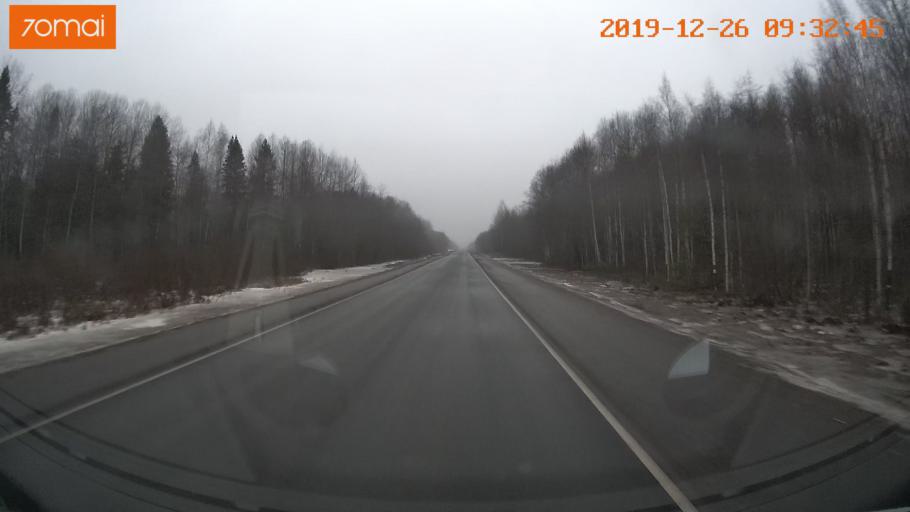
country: RU
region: Vologda
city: Gryazovets
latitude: 59.0817
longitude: 40.1114
